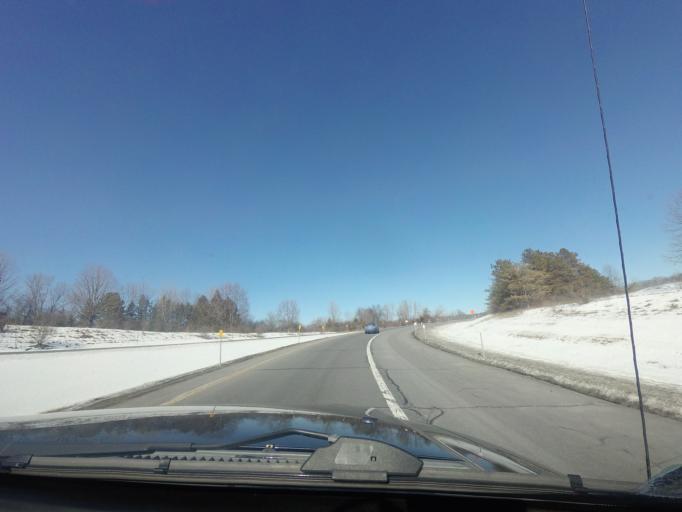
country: US
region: New York
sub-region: Rensselaer County
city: East Greenbush
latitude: 42.5592
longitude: -73.6821
